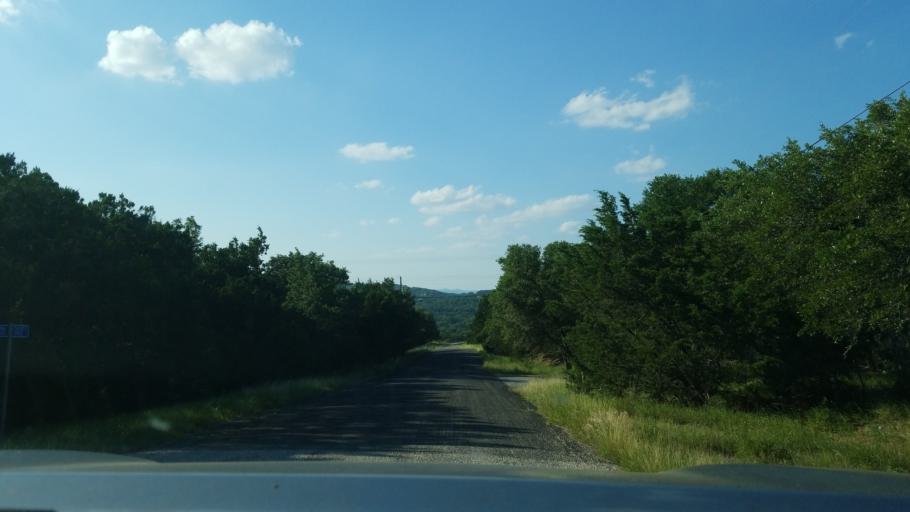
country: US
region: Texas
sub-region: Comal County
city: Bulverde
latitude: 29.7818
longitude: -98.4414
